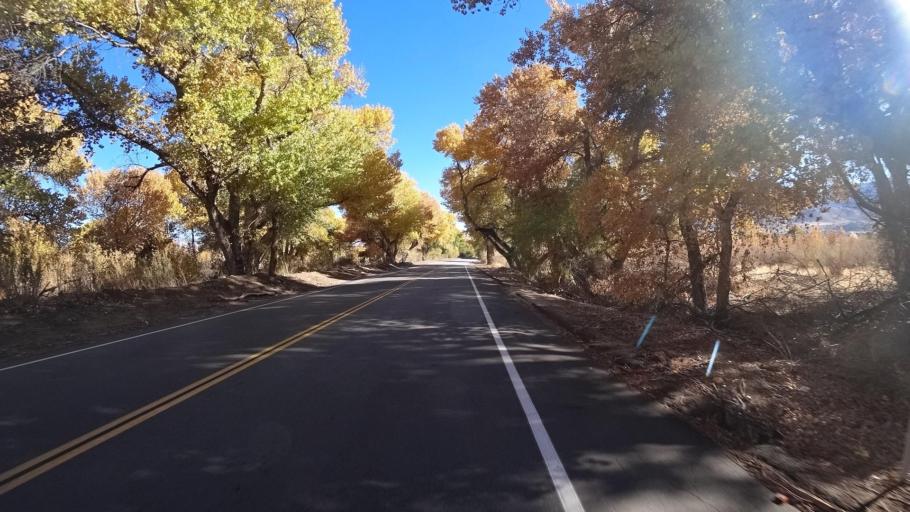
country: US
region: California
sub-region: Kern County
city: Weldon
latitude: 35.6714
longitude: -118.3256
